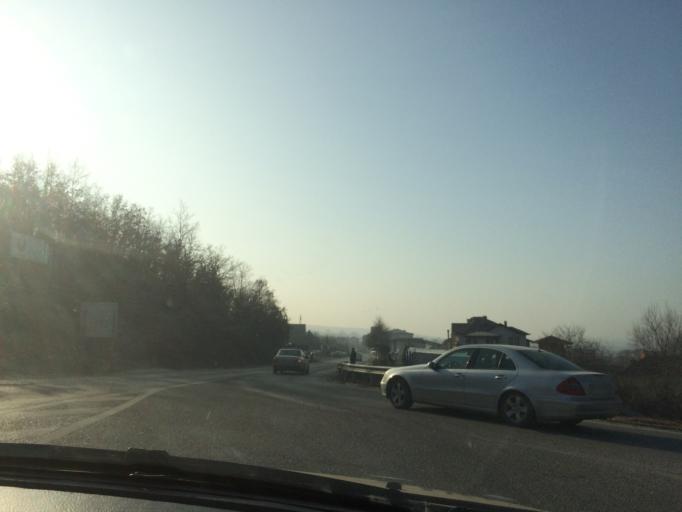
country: XK
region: Pec
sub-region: Komuna e Klines
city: Klina
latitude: 42.5911
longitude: 20.5839
